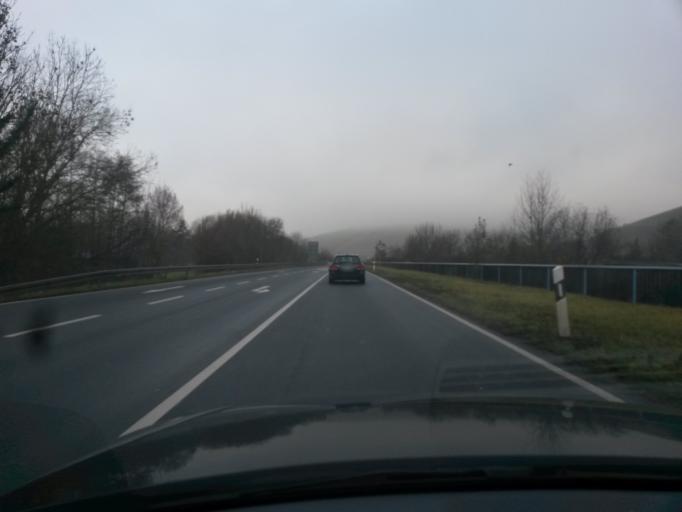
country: DE
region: Bavaria
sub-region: Regierungsbezirk Unterfranken
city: Randersacker
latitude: 49.7530
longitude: 9.9846
